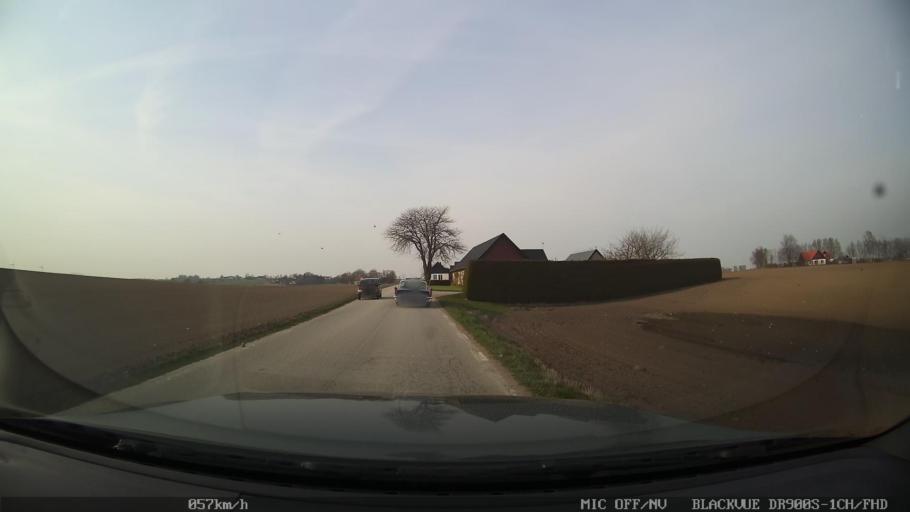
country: SE
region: Skane
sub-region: Ystads Kommun
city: Ystad
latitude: 55.4597
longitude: 13.8263
